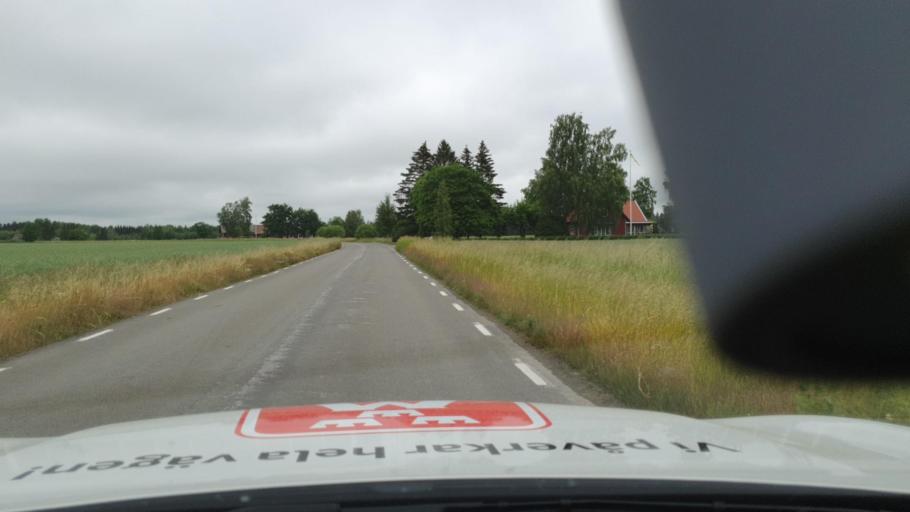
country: SE
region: Vaestra Goetaland
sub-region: Tidaholms Kommun
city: Olofstorp
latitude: 58.3728
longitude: 14.0082
